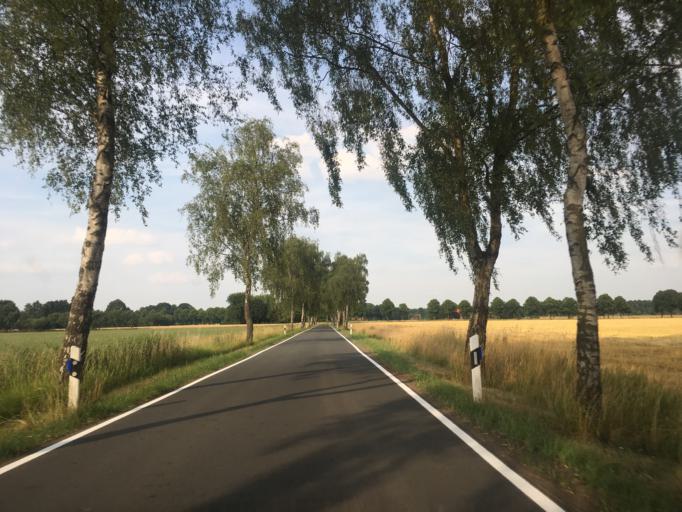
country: DE
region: North Rhine-Westphalia
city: Ludinghausen
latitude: 51.8053
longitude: 7.3939
